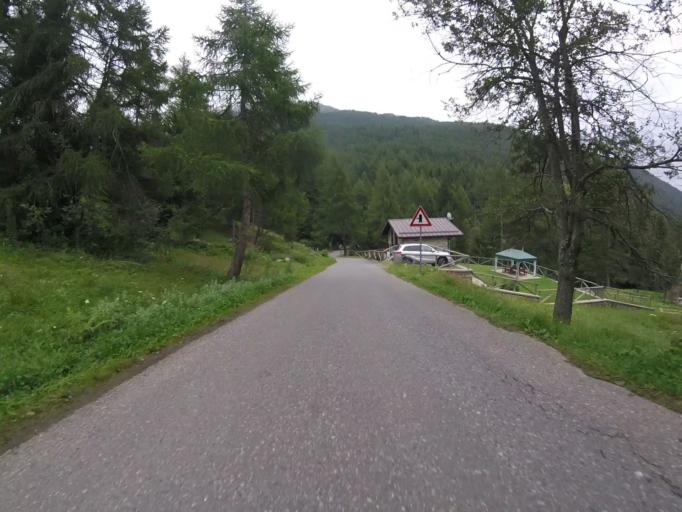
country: IT
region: Lombardy
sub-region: Provincia di Brescia
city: Monno
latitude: 46.2437
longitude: 10.3177
